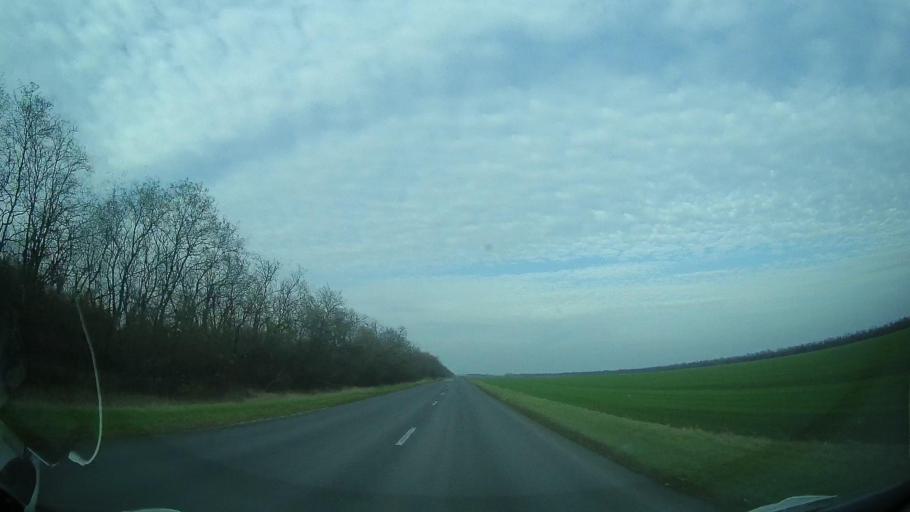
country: RU
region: Rostov
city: Zernograd
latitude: 46.9460
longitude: 40.3666
